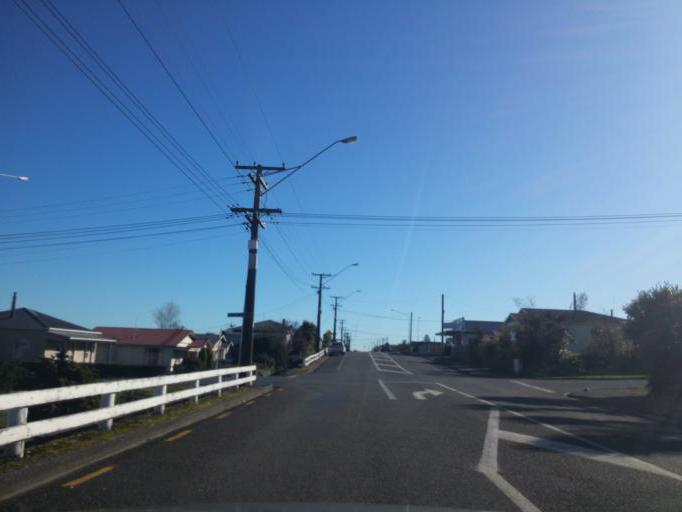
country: NZ
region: West Coast
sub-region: Grey District
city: Greymouth
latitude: -42.4433
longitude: 171.2127
